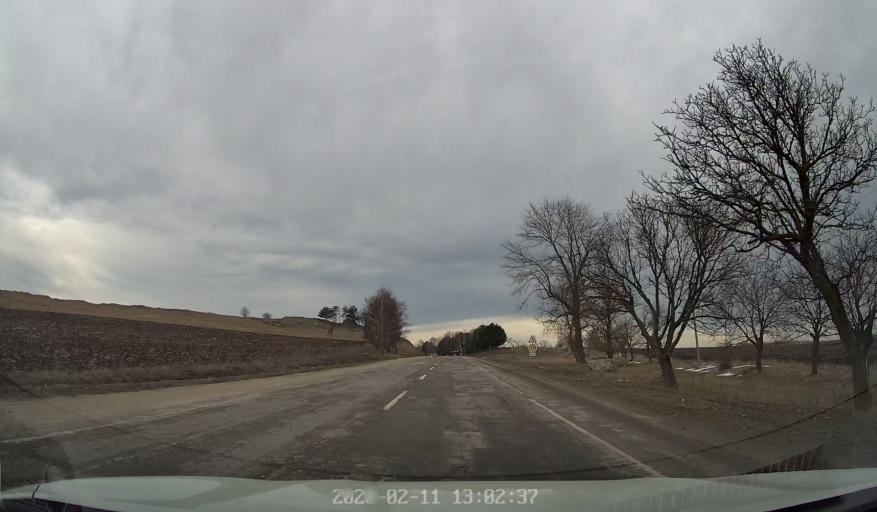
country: MD
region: Briceni
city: Briceni
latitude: 48.3166
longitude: 26.9765
